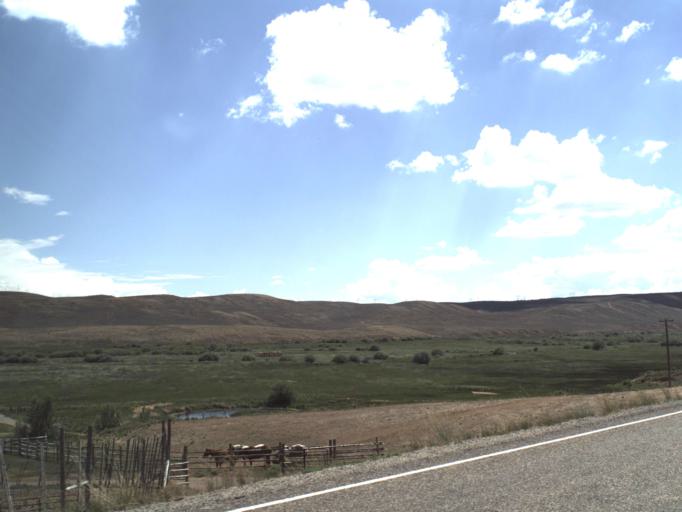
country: US
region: Utah
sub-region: Rich County
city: Randolph
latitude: 41.5170
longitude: -111.2103
